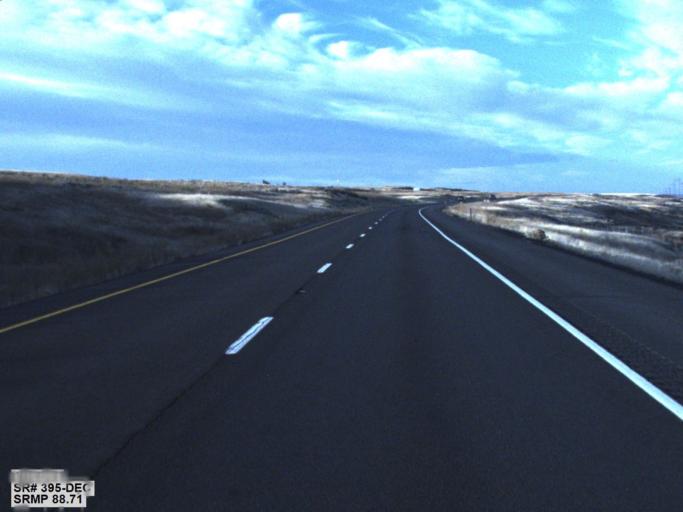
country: US
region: Washington
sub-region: Adams County
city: Ritzville
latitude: 47.0300
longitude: -118.4665
